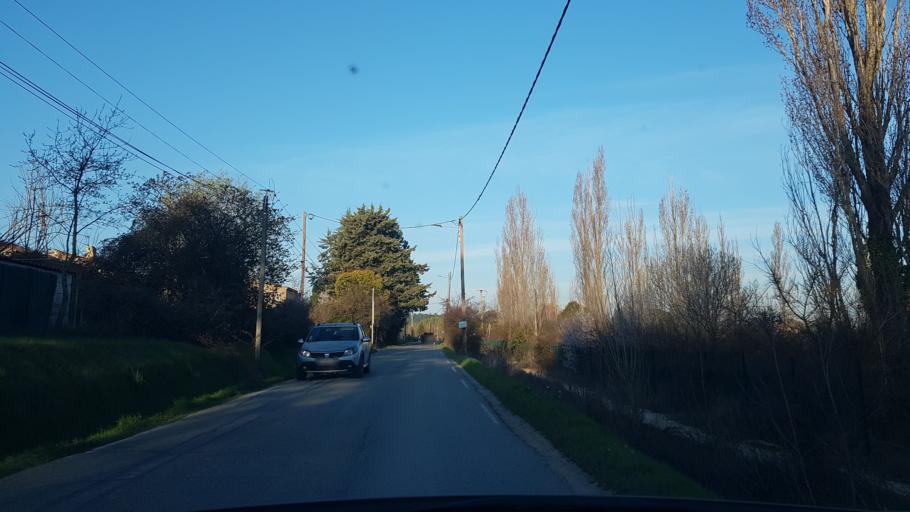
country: FR
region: Provence-Alpes-Cote d'Azur
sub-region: Departement des Bouches-du-Rhone
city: Cabries
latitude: 43.4488
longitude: 5.3869
